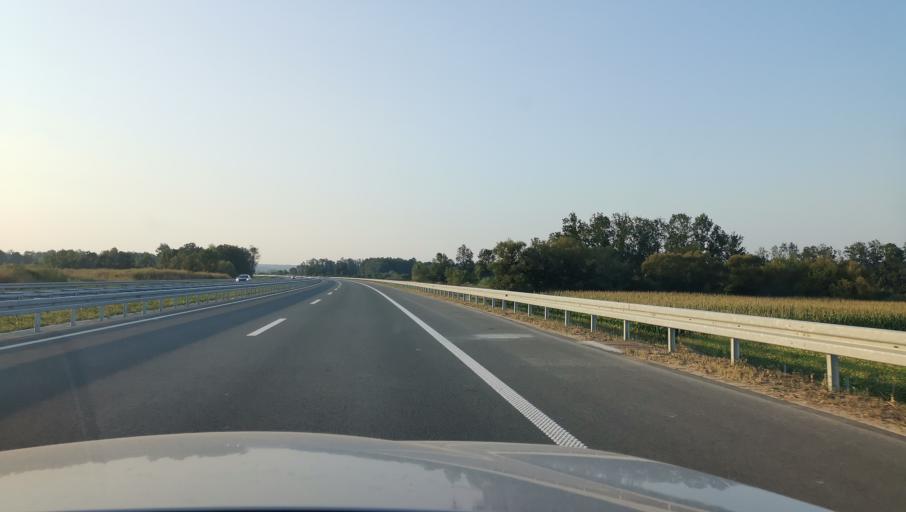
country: RS
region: Central Serbia
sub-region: Kolubarski Okrug
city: Ljig
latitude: 44.2640
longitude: 20.2708
